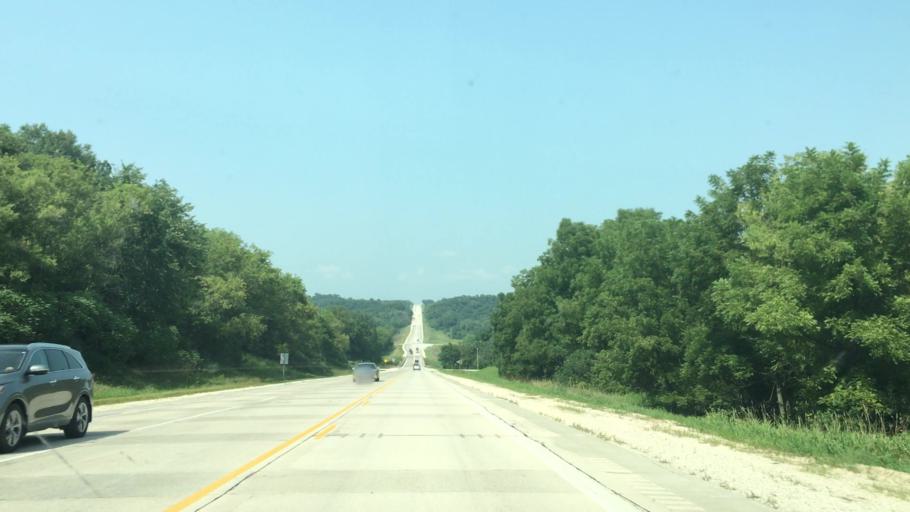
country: US
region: Iowa
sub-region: Winneshiek County
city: Decorah
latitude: 43.3120
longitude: -91.8147
